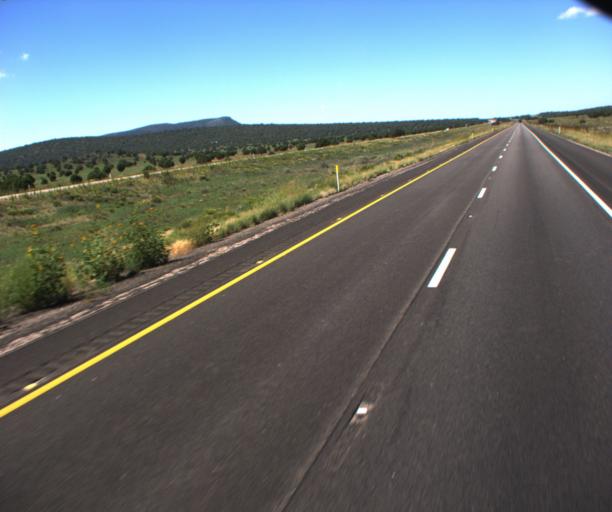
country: US
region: Arizona
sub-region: Mohave County
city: Peach Springs
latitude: 35.2325
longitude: -113.2180
